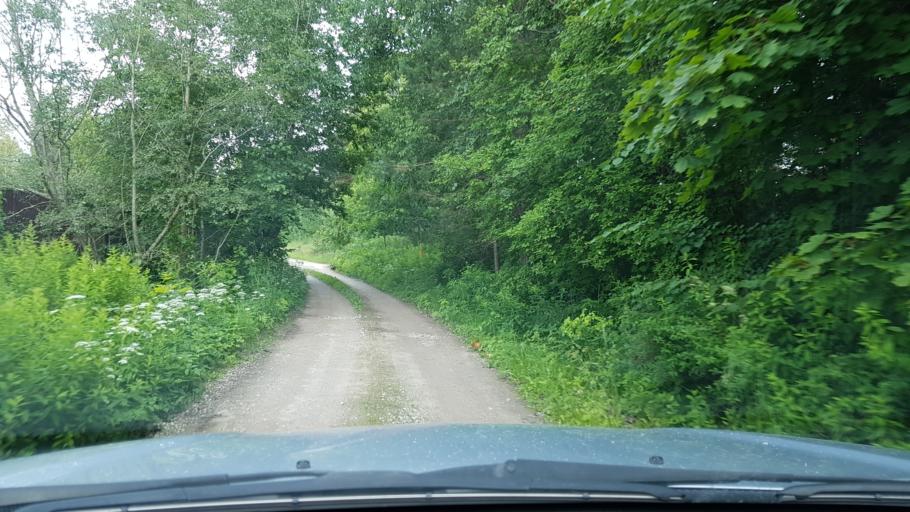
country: EE
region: Ida-Virumaa
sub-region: Narva-Joesuu linn
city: Narva-Joesuu
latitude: 59.4535
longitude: 28.0770
